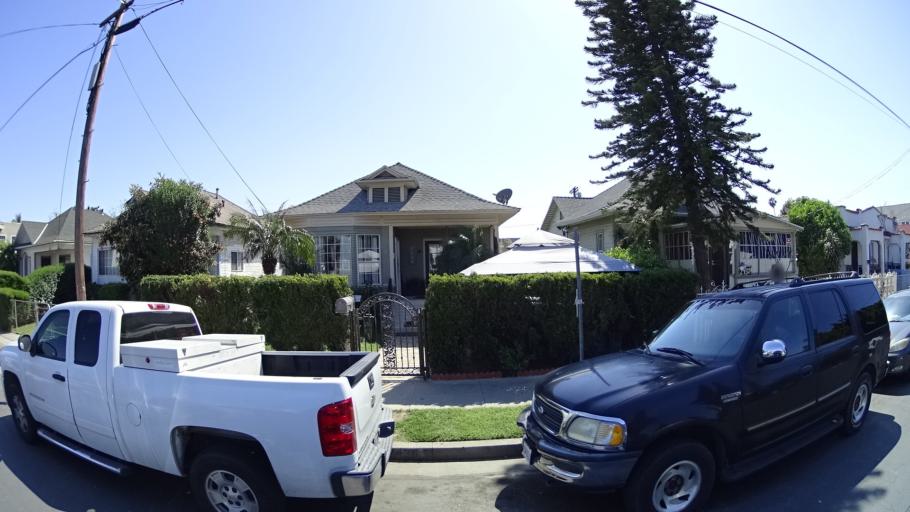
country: US
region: California
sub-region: Los Angeles County
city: Boyle Heights
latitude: 34.0490
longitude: -118.2051
